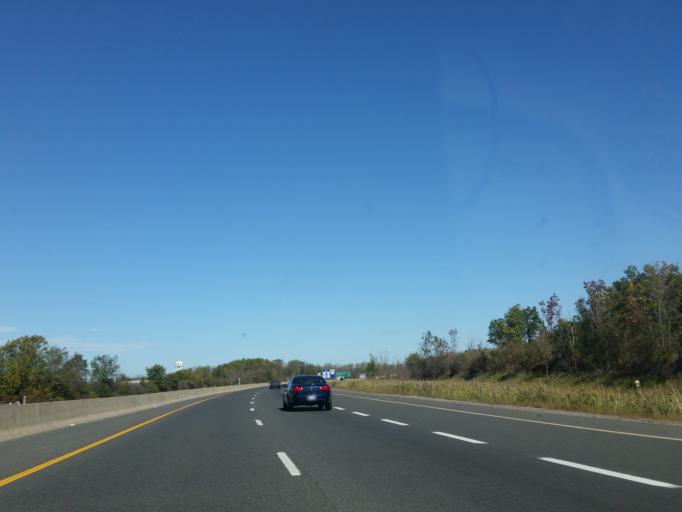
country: CA
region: Ontario
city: Niagara Falls
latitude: 43.0365
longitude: -79.1175
